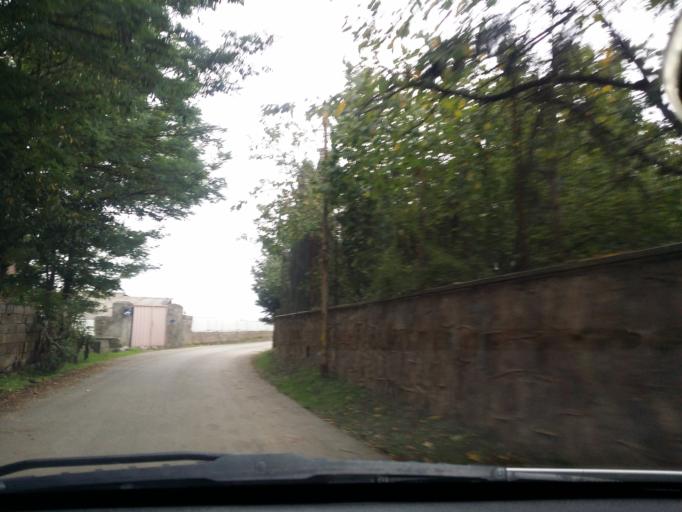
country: IR
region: Mazandaran
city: Chalus
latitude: 36.5103
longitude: 51.2296
